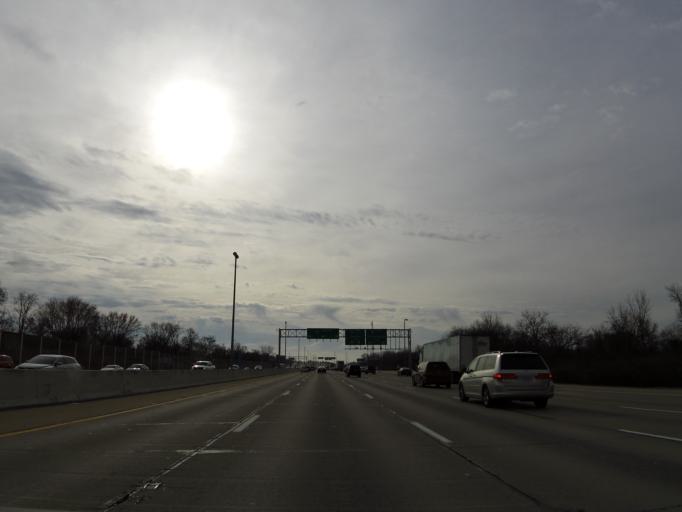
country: US
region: Indiana
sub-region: Marion County
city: Lawrence
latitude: 39.8177
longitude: -86.0311
